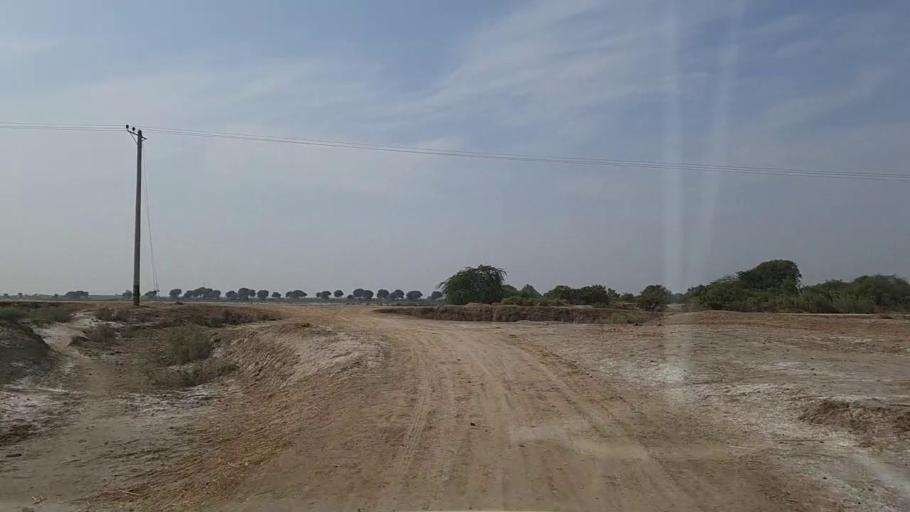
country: PK
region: Sindh
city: Mirpur Batoro
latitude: 24.6084
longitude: 68.2097
